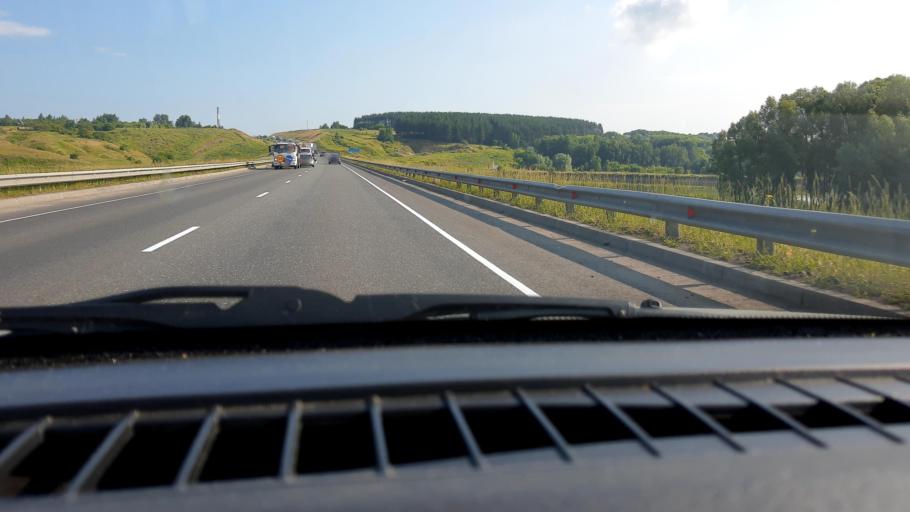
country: RU
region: Nizjnij Novgorod
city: Kstovo
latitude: 56.0757
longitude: 44.1329
